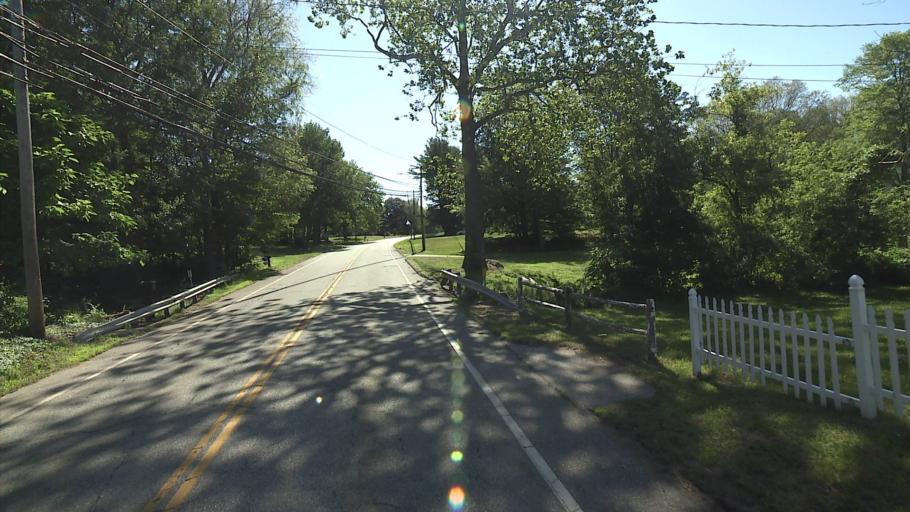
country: US
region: Connecticut
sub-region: Middlesex County
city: East Hampton
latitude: 41.5678
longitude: -72.4915
